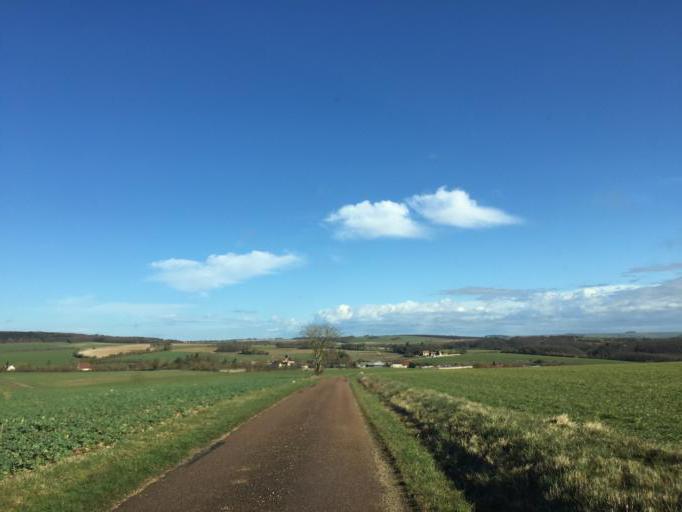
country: FR
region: Bourgogne
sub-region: Departement de l'Yonne
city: Fontenailles
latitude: 47.5511
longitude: 3.3305
